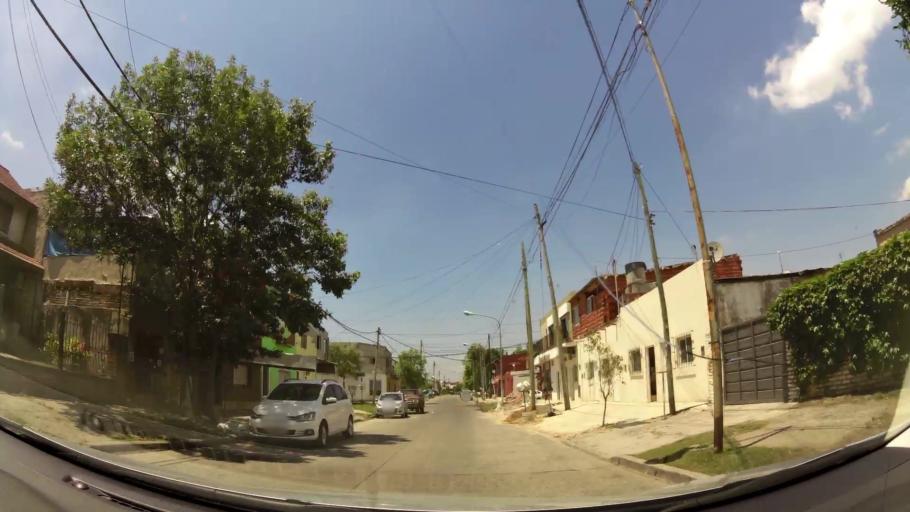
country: AR
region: Buenos Aires
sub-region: Partido de Tigre
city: Tigre
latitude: -34.4139
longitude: -58.6009
